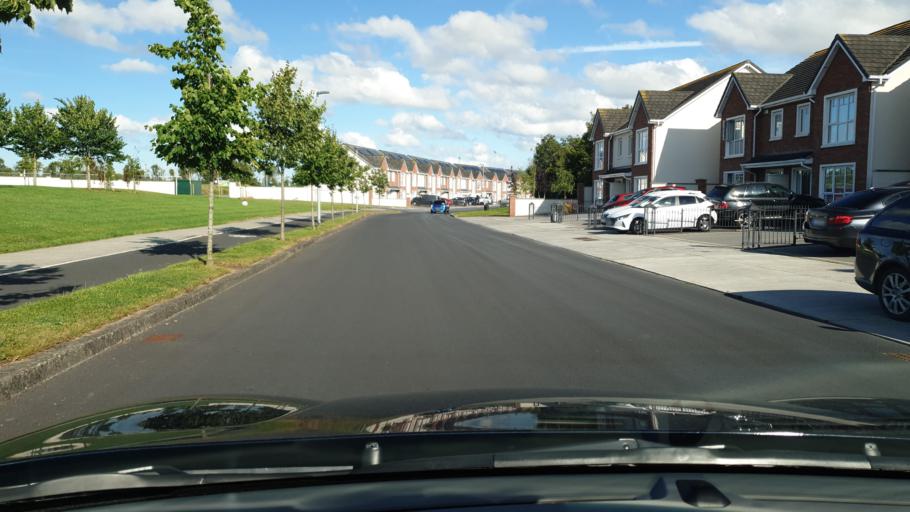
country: IE
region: Leinster
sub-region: An Mhi
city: Ashbourne
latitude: 53.5112
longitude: -6.3897
